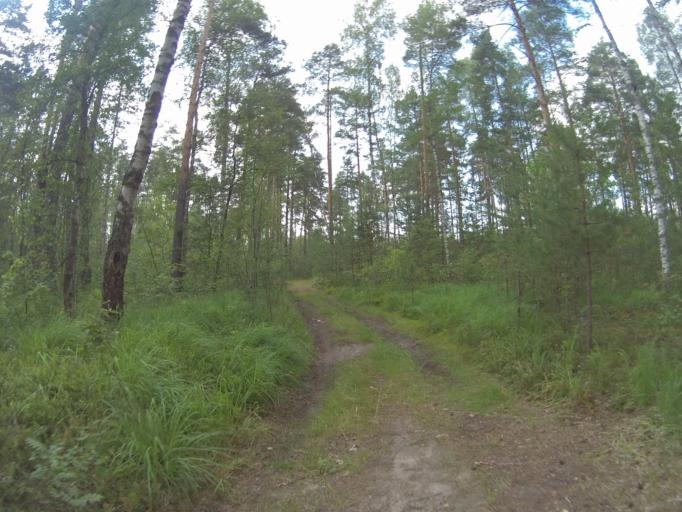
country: RU
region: Vladimir
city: Vorsha
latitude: 56.0074
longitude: 40.1347
